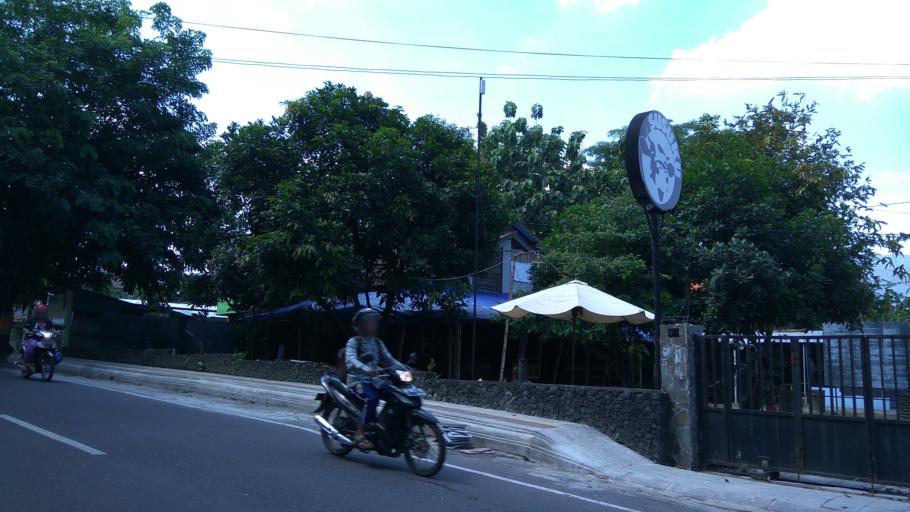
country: ID
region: Central Java
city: Ungaran
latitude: -7.1357
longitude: 110.4097
